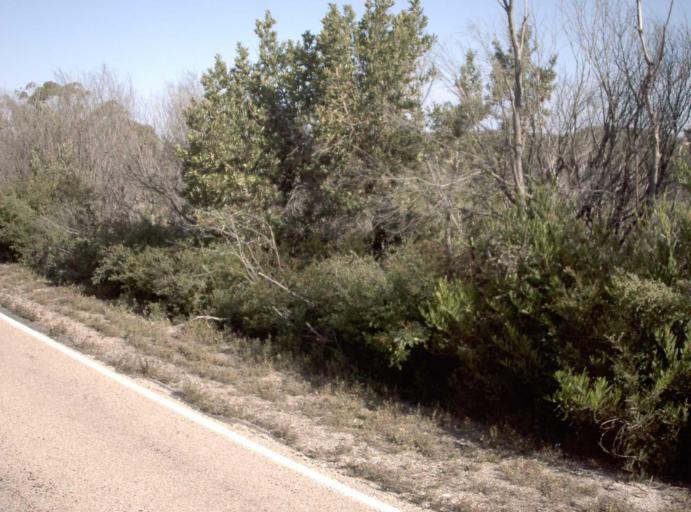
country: AU
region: Victoria
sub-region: East Gippsland
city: Lakes Entrance
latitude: -37.7975
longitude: 148.7049
